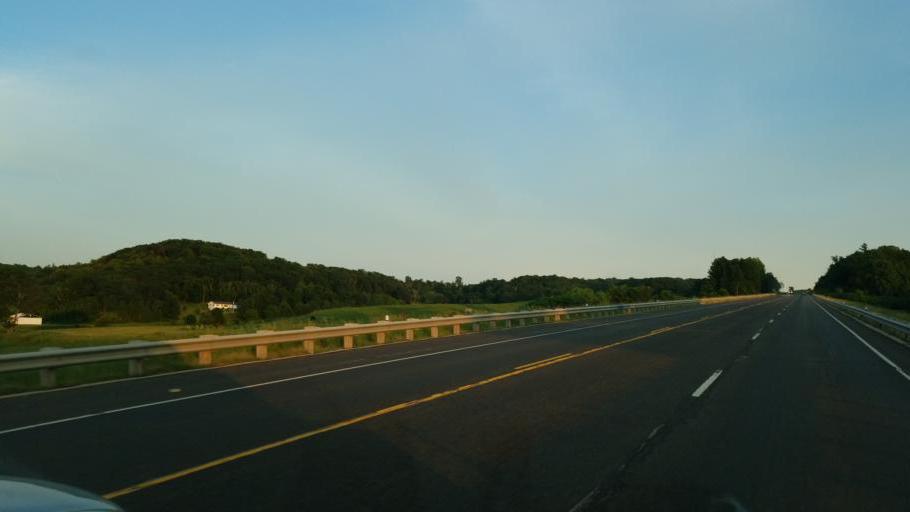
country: US
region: Wisconsin
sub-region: Monroe County
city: Tomah
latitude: 43.9112
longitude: -90.4939
